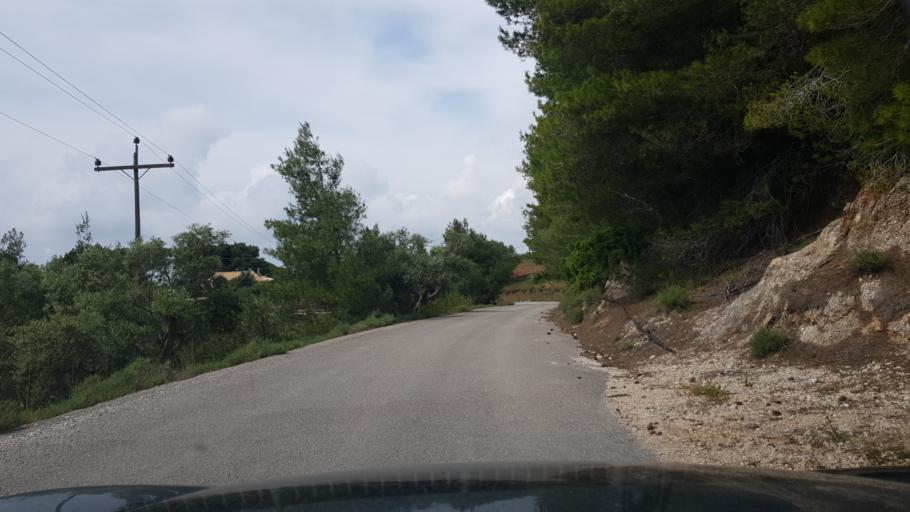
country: GR
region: Ionian Islands
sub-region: Lefkada
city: Nidri
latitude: 38.6266
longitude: 20.5639
